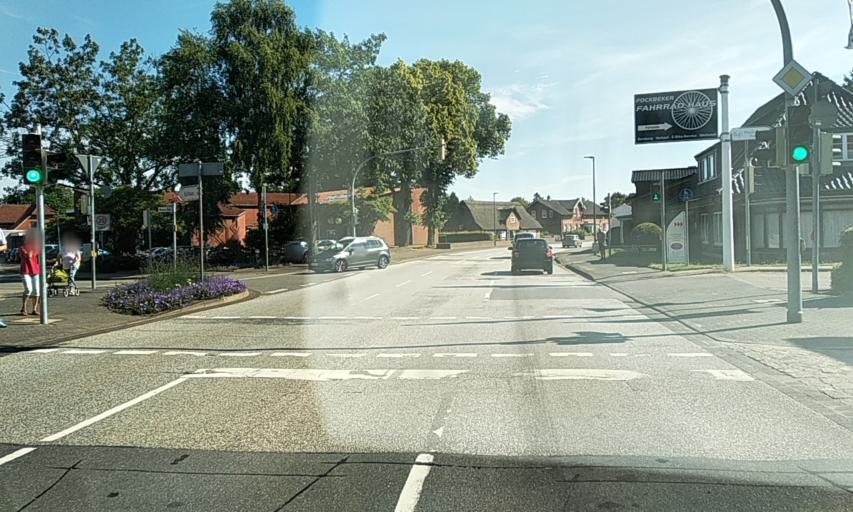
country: DE
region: Schleswig-Holstein
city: Fockbek
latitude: 54.3068
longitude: 9.6030
